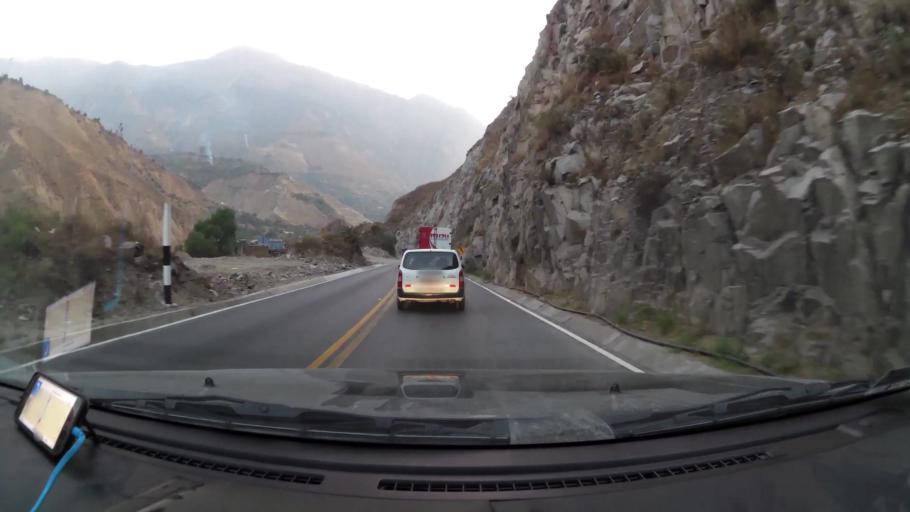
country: PE
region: Lima
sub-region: Provincia de Huarochiri
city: Surco
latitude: -11.8775
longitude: -76.4325
